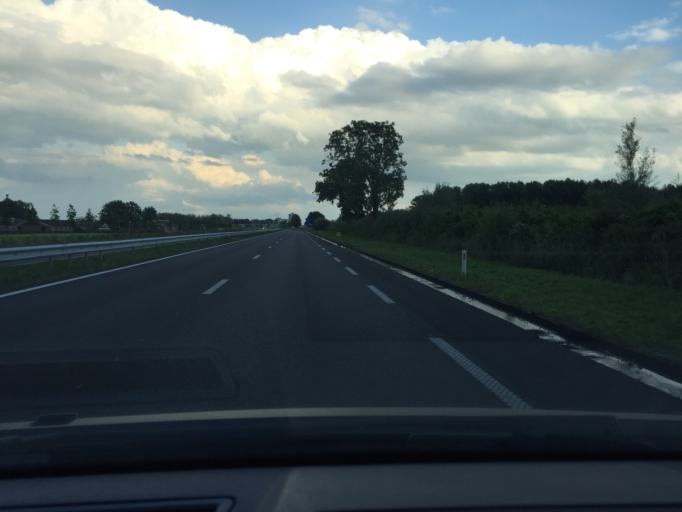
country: NL
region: North Brabant
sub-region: Gemeente Veghel
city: Eerde
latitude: 51.6368
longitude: 5.4796
